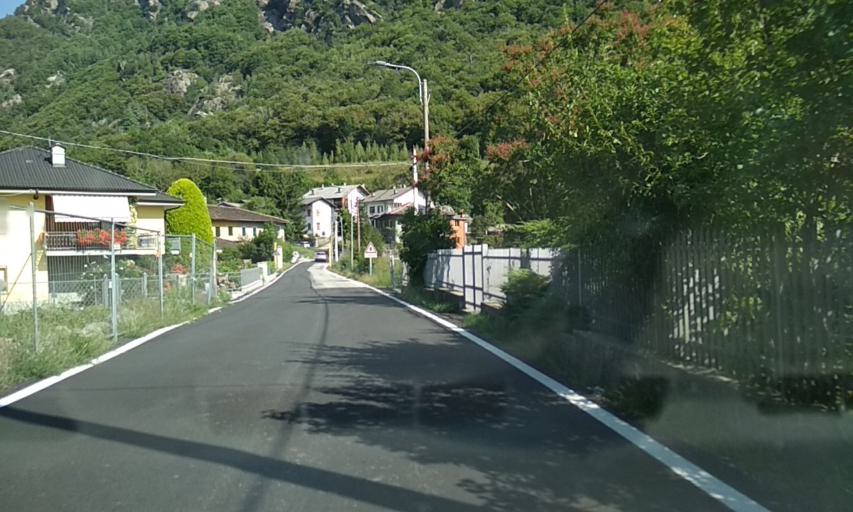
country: IT
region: Piedmont
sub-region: Provincia di Torino
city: Locana
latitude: 45.4296
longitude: 7.4348
